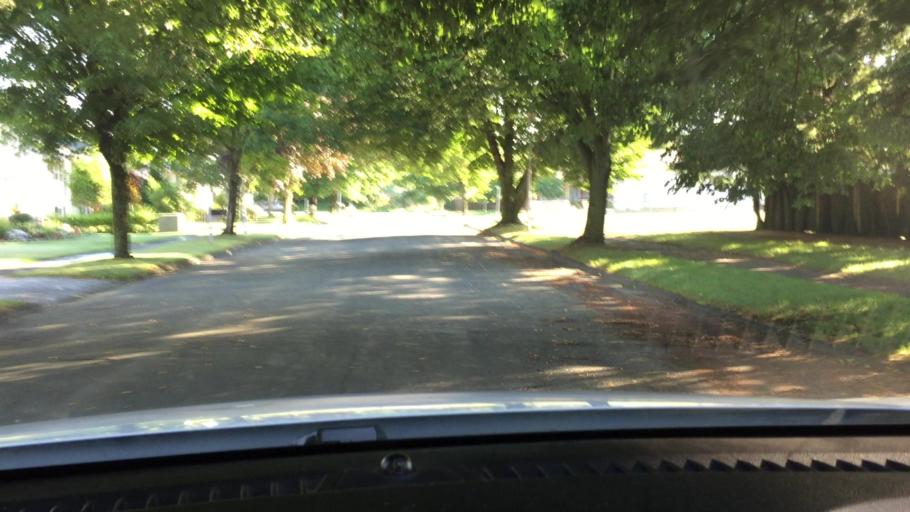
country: US
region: Massachusetts
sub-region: Berkshire County
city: Pittsfield
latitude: 42.4187
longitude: -73.2347
